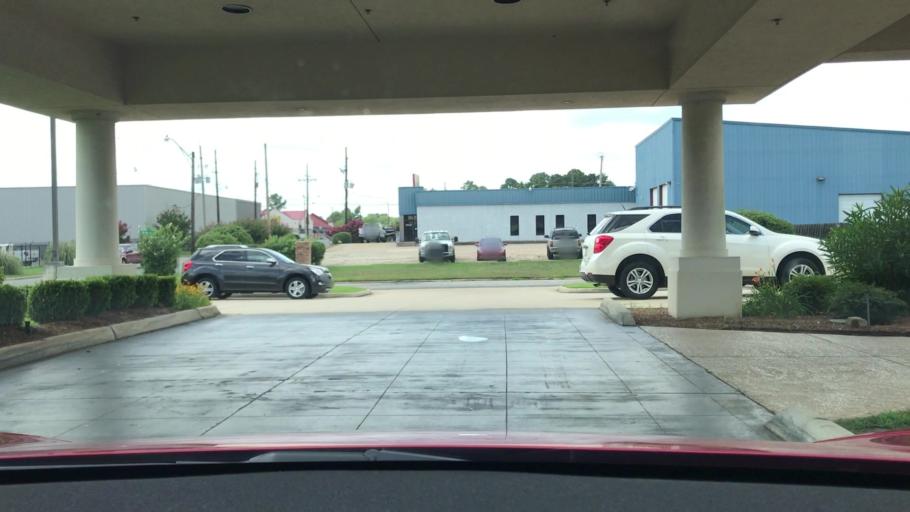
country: US
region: Louisiana
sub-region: De Soto Parish
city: Stonewall
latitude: 32.3987
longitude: -93.8052
